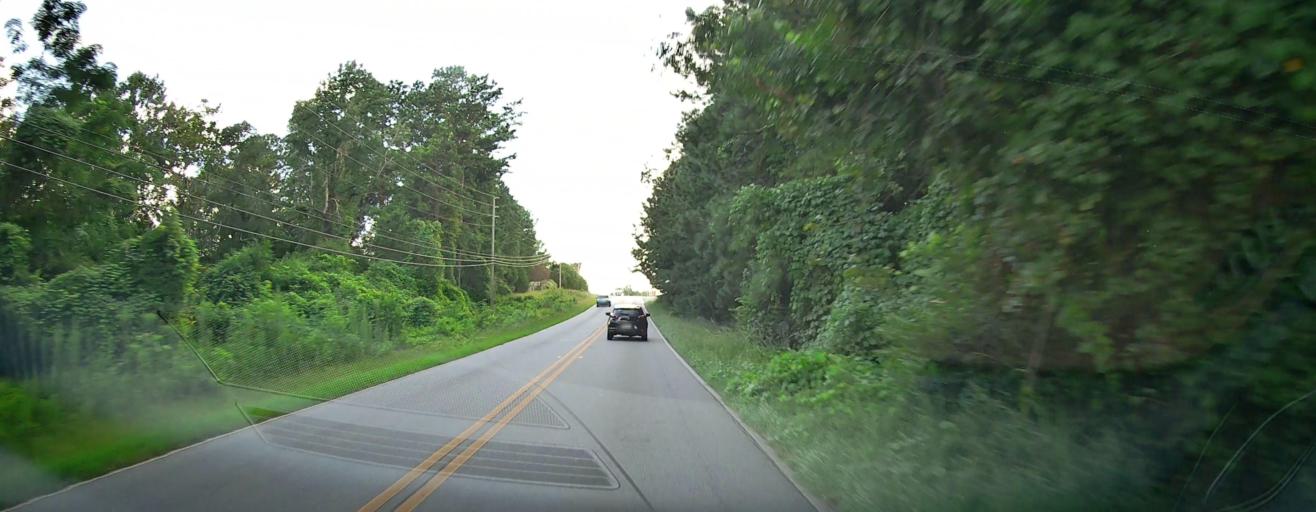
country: US
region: Georgia
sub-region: Muscogee County
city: Columbus
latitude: 32.5379
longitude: -84.9019
